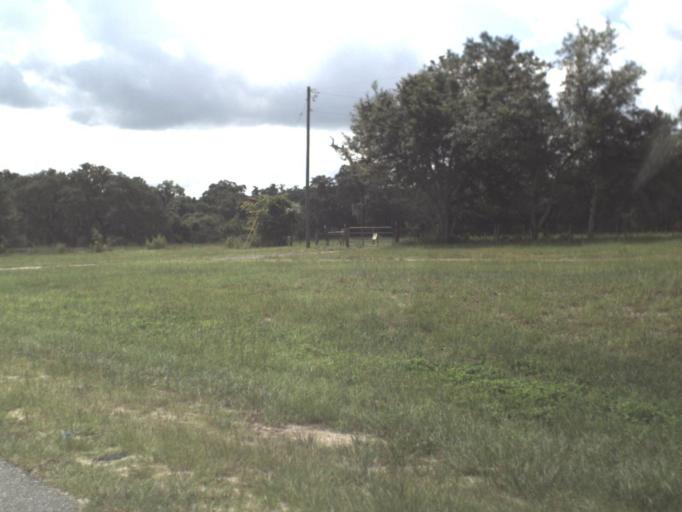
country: US
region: Florida
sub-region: Hernando County
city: Ridge Manor
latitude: 28.5076
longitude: -82.1602
